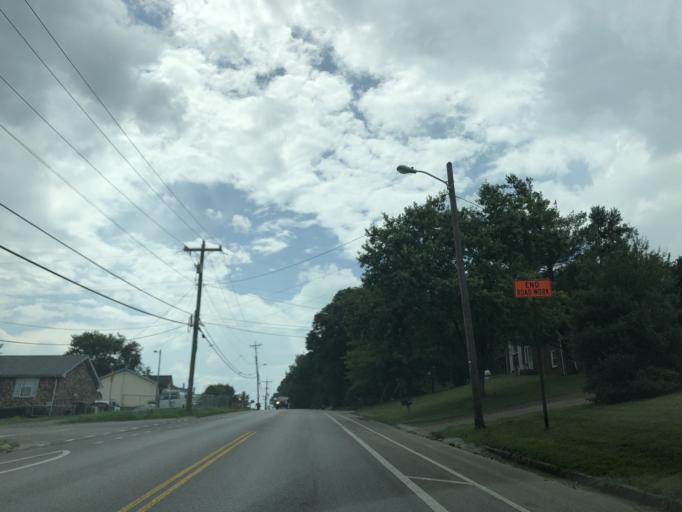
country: US
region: Tennessee
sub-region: Williamson County
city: Brentwood Estates
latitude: 36.0526
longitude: -86.6851
